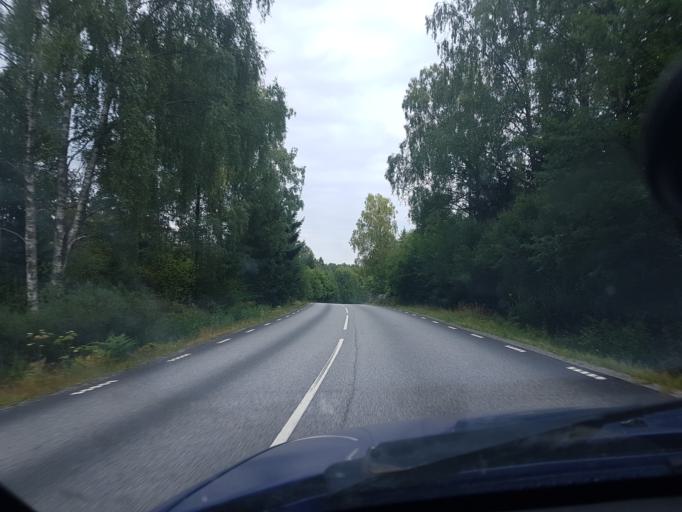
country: SE
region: Vaestra Goetaland
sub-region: Lysekils Kommun
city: Lysekil
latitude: 58.2722
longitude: 11.5328
